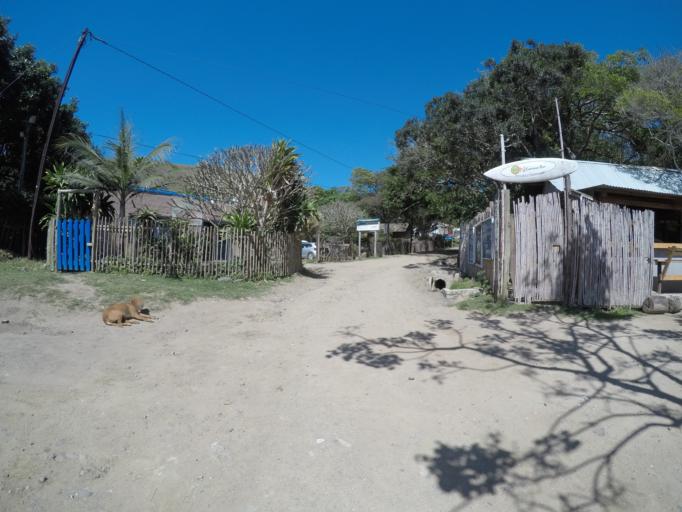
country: ZA
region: Eastern Cape
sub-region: OR Tambo District Municipality
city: Libode
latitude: -31.9884
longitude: 29.1469
